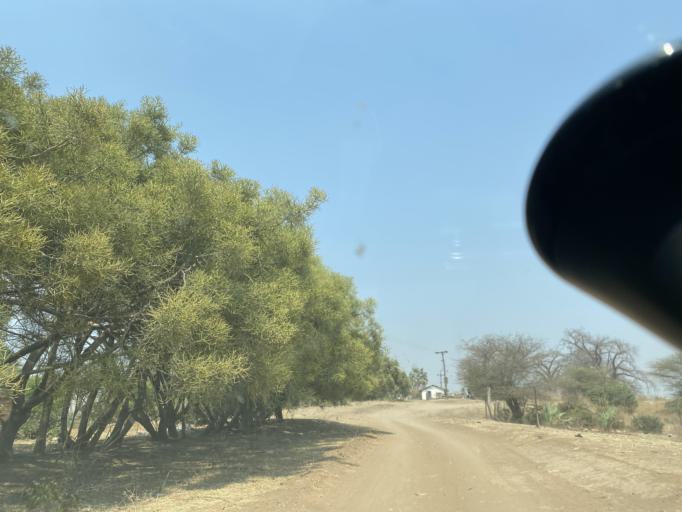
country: ZW
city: Chirundu
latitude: -16.1596
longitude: 28.8054
